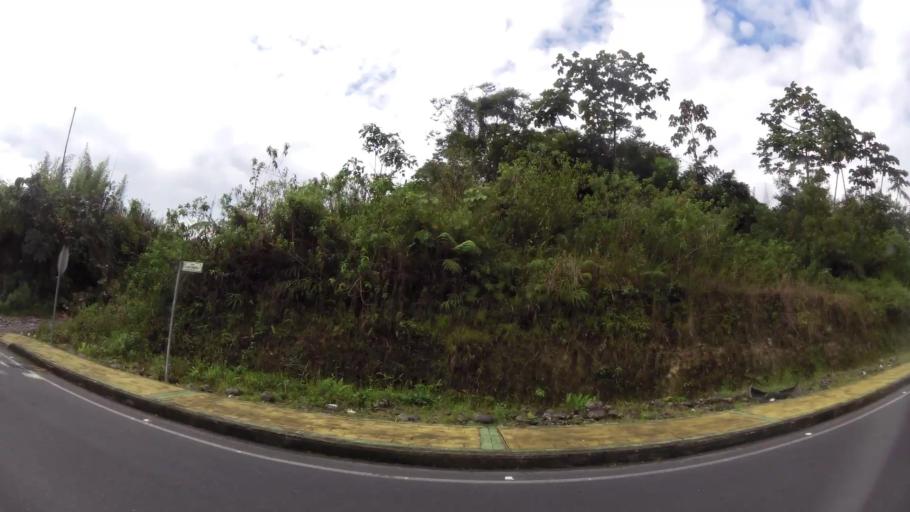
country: EC
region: Pastaza
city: Puyo
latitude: -1.4844
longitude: -77.9957
